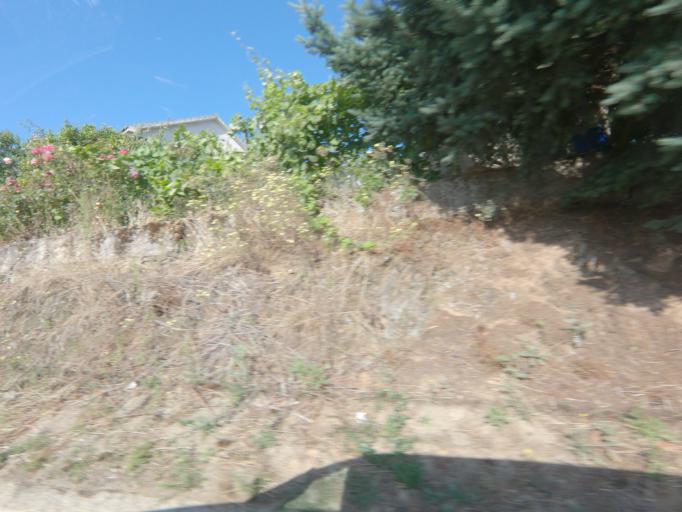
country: PT
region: Vila Real
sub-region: Sabrosa
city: Sabrosa
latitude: 41.2523
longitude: -7.5798
